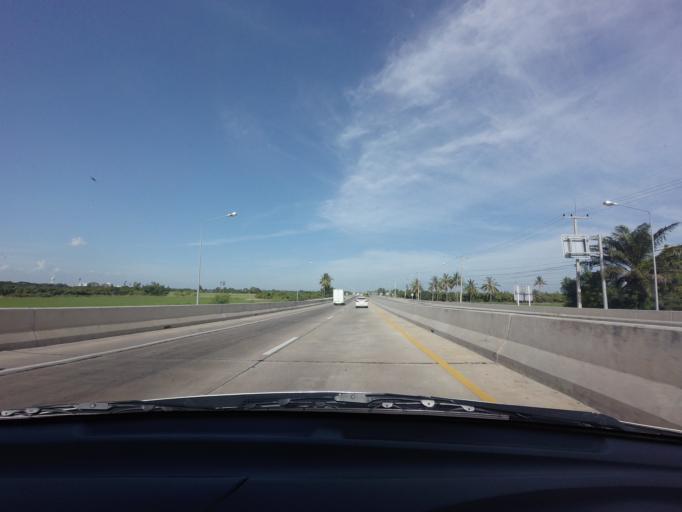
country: TH
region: Suphan Buri
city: Suphan Buri
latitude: 14.4524
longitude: 100.0924
